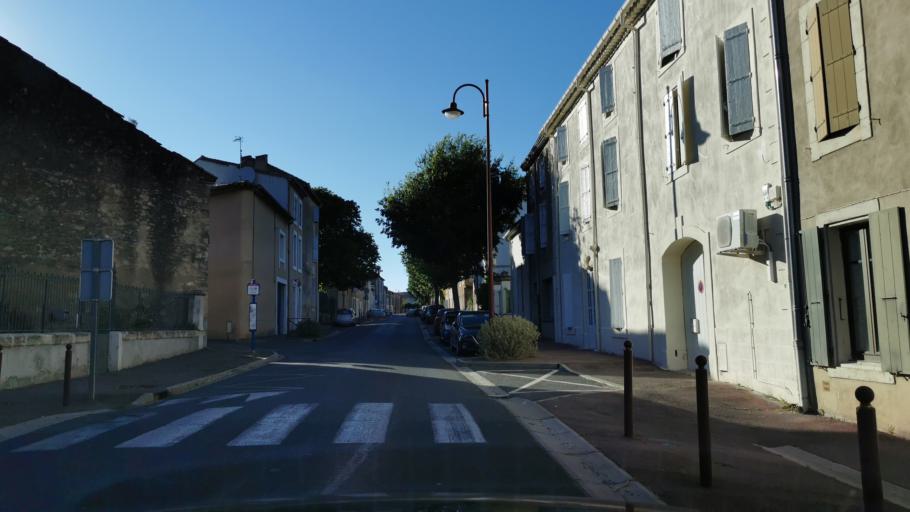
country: FR
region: Languedoc-Roussillon
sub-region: Departement de l'Aude
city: Ouveillan
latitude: 43.2873
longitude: 2.9738
